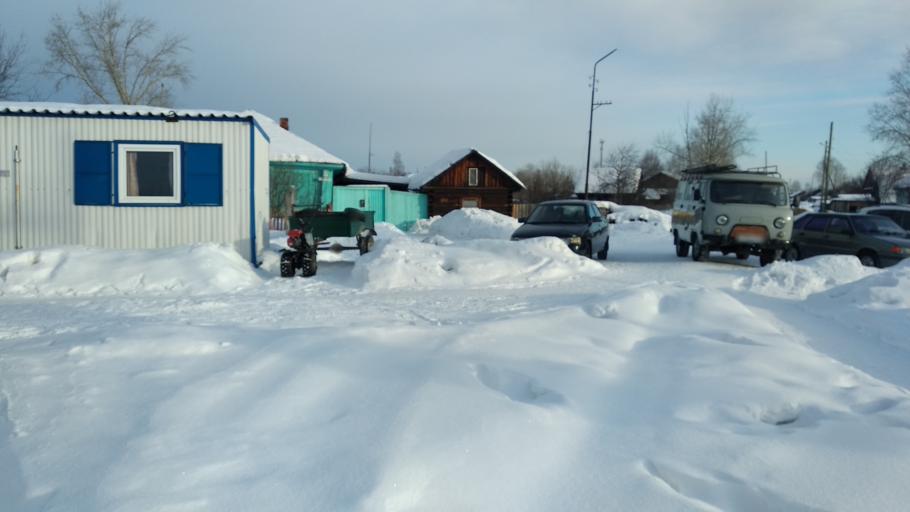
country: RU
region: Sverdlovsk
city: Serov
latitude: 59.9233
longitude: 60.5749
